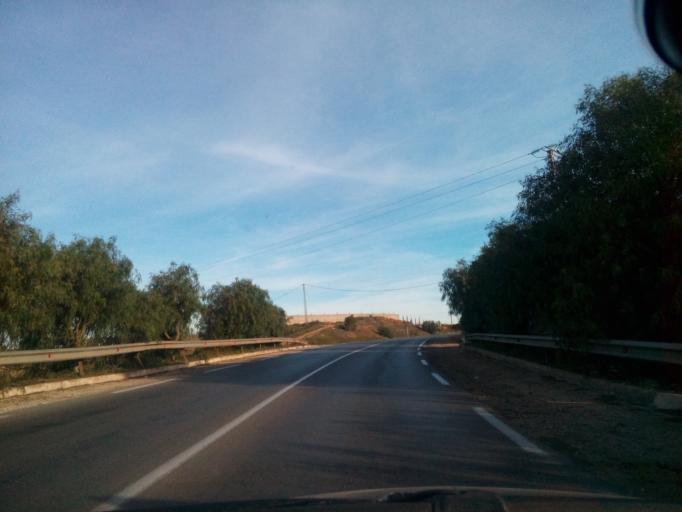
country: DZ
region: Mostaganem
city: Mostaganem
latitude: 35.8520
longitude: 0.1649
